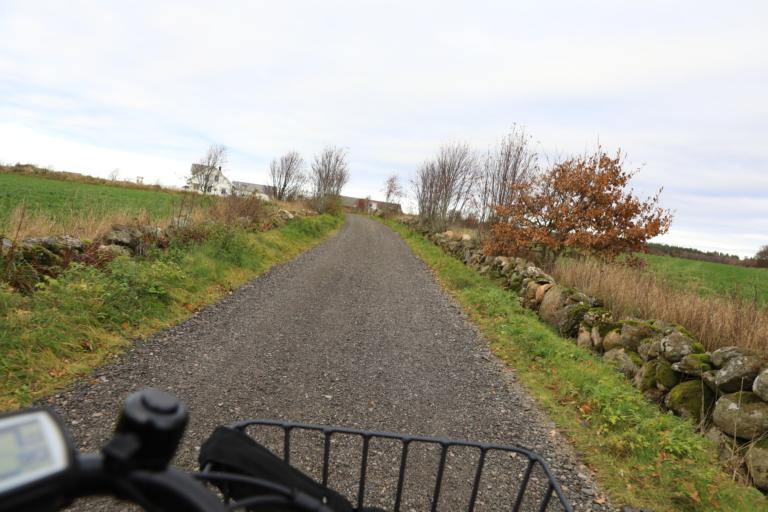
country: SE
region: Halland
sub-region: Varbergs Kommun
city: Traslovslage
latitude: 57.0524
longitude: 12.3384
